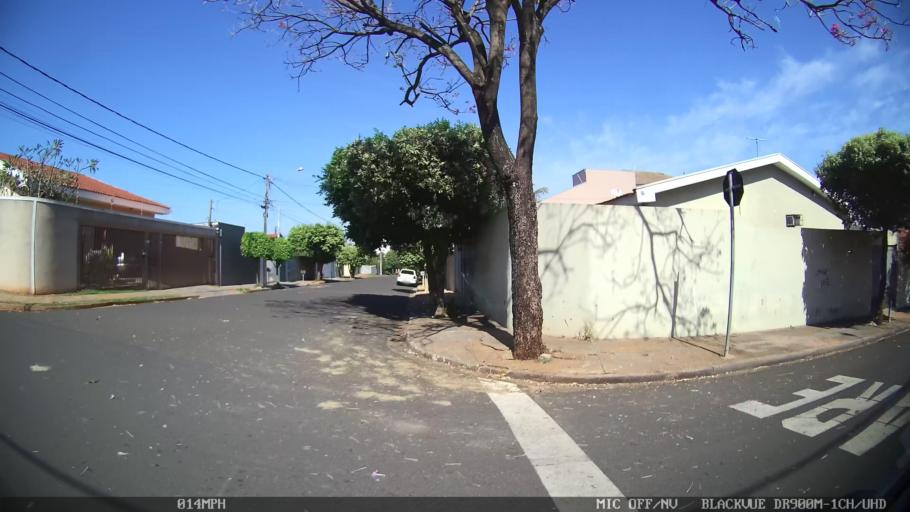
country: BR
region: Sao Paulo
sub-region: Sao Jose Do Rio Preto
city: Sao Jose do Rio Preto
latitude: -20.7823
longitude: -49.3757
